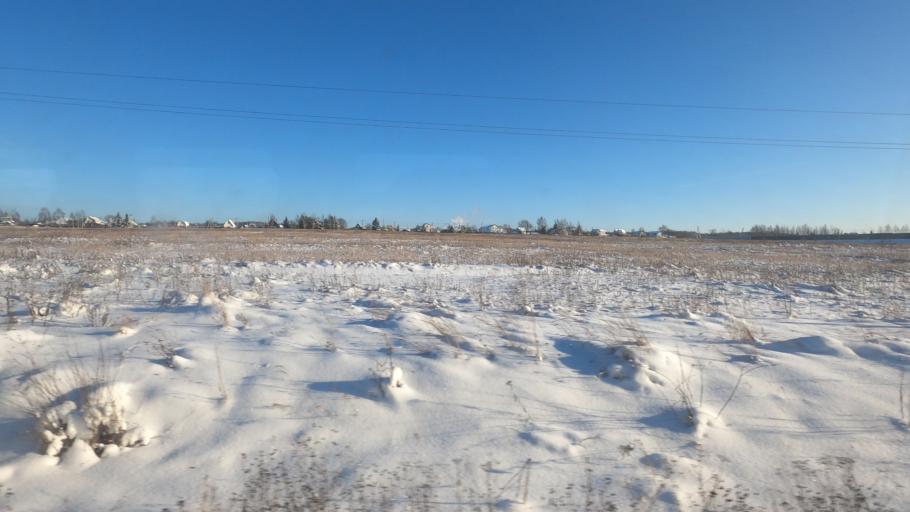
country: RU
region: Moskovskaya
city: Orud'yevo
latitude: 56.4103
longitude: 37.4963
